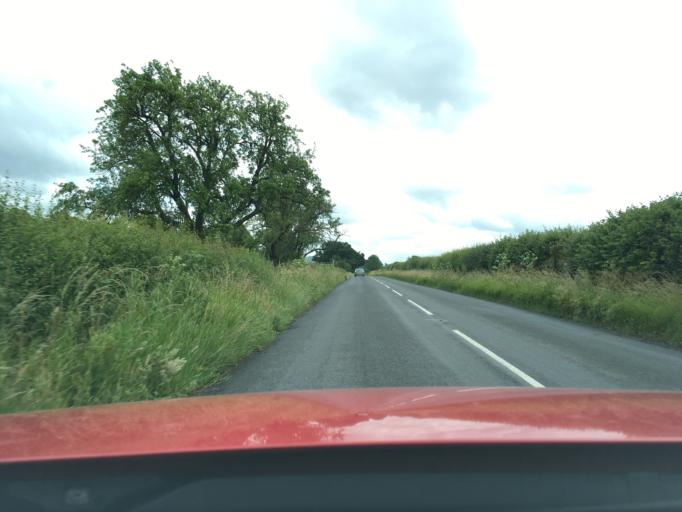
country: GB
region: England
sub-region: Gloucestershire
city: Winchcombe
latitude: 52.0155
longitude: -1.9587
